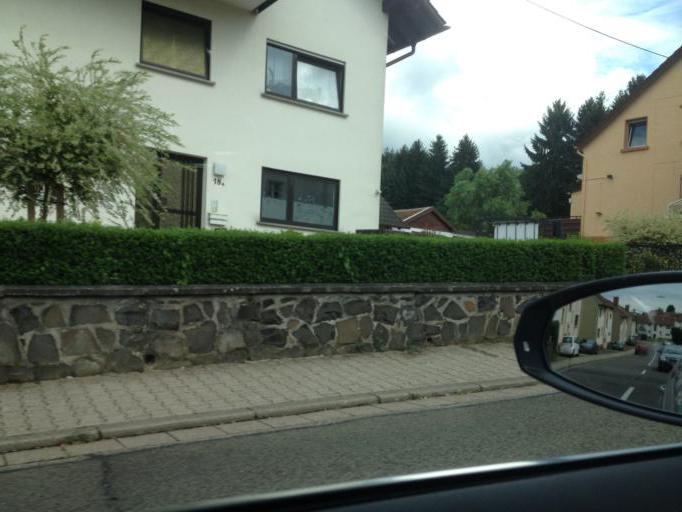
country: DE
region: Saarland
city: Schiffweiler
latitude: 49.3587
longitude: 7.1127
